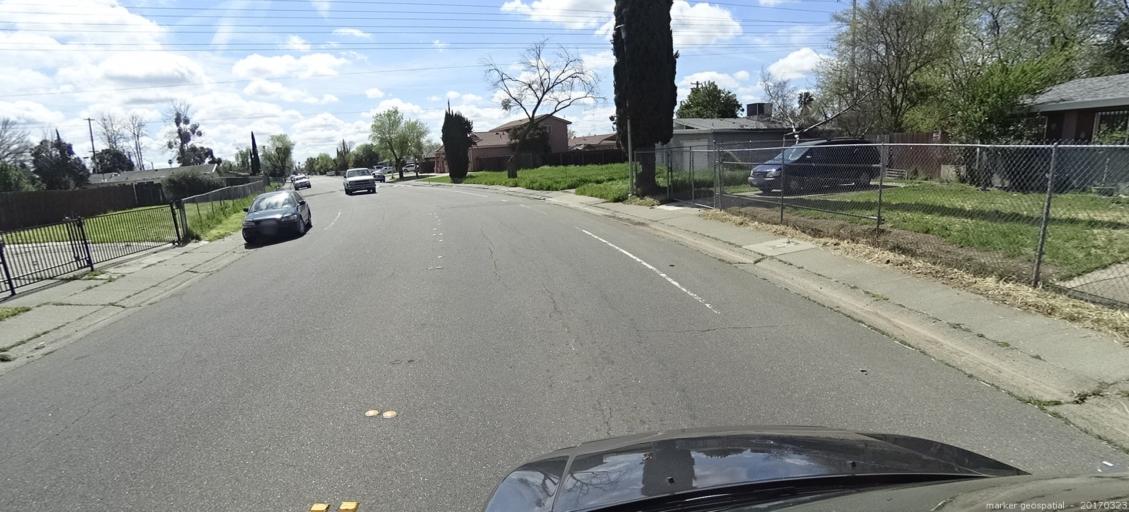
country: US
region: California
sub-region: Sacramento County
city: Florin
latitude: 38.5092
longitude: -121.4164
